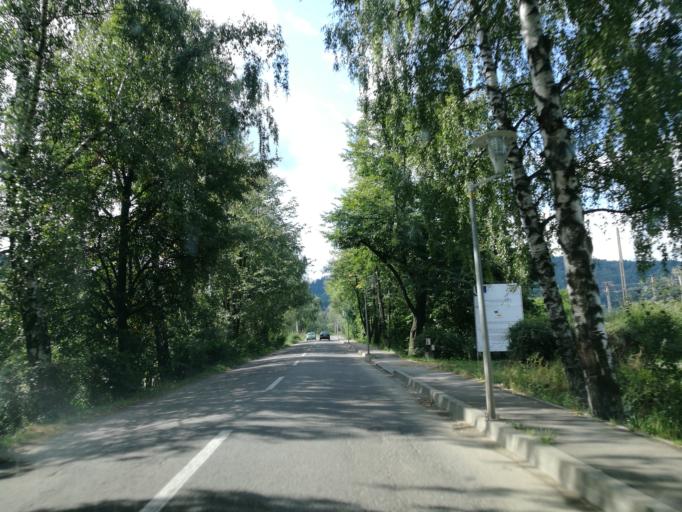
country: RO
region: Suceava
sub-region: Oras Gura Humorului
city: Gura Humorului
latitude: 47.5439
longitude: 25.8701
